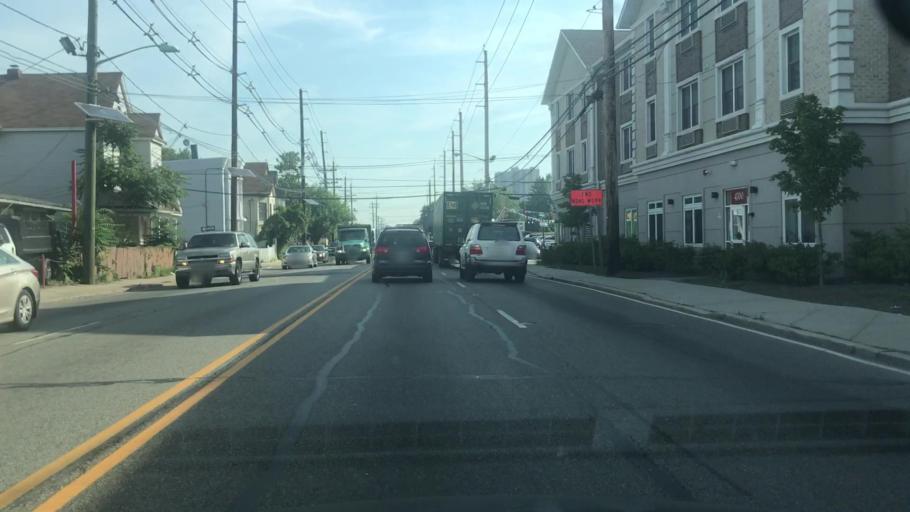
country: US
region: New Jersey
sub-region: Hudson County
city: Union City
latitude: 40.7856
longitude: -74.0326
